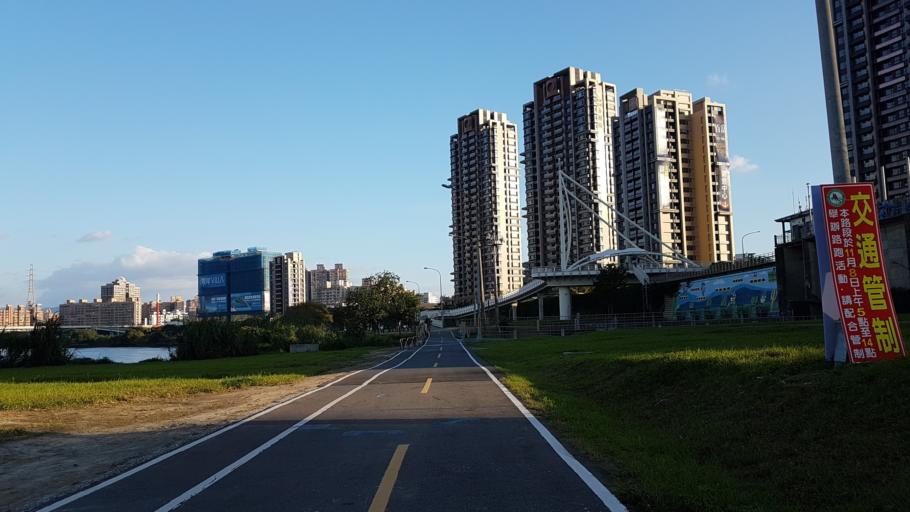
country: TW
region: Taipei
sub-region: Taipei
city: Banqiao
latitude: 25.0110
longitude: 121.4896
